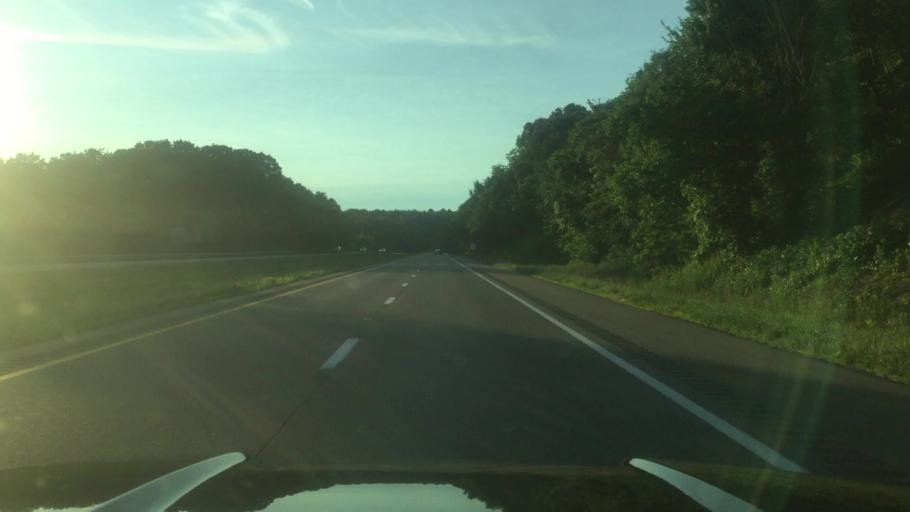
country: US
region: Ohio
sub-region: Tuscarawas County
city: Newcomerstown
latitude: 40.3020
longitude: -81.5628
